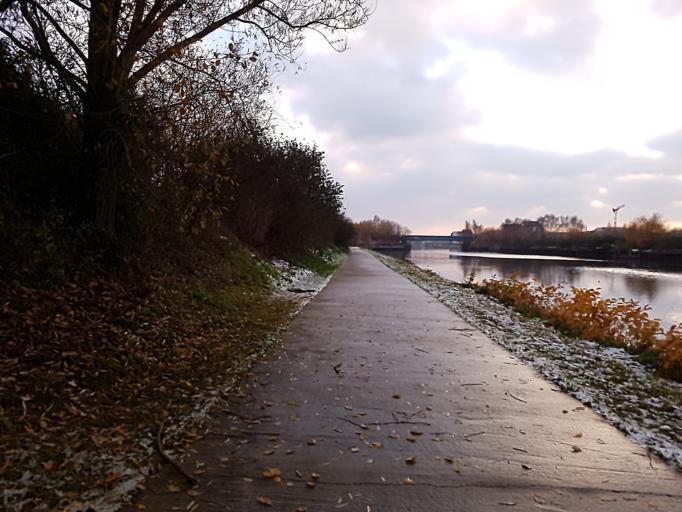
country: FR
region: Nord-Pas-de-Calais
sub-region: Departement du Nord
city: Saint-Andre-lez-Lille
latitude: 50.6635
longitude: 3.0617
